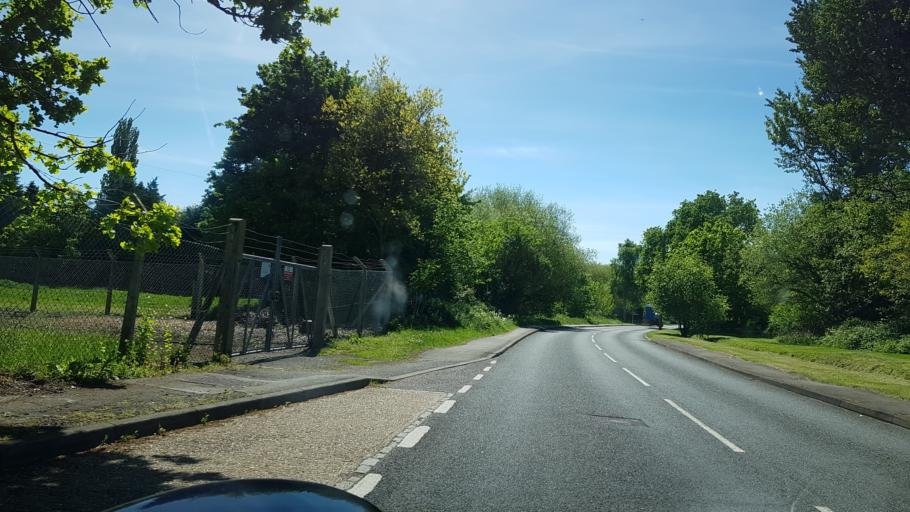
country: GB
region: England
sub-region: Surrey
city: Guildford
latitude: 51.2654
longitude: -0.5694
